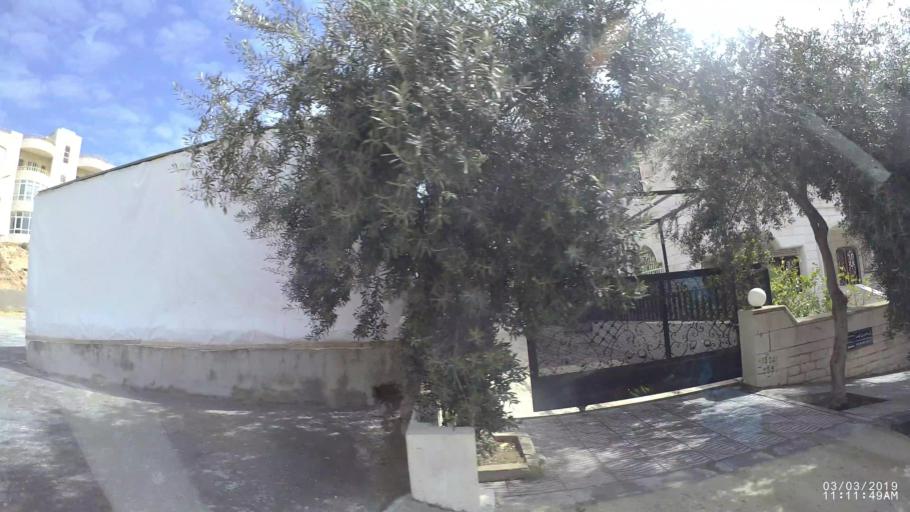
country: JO
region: Amman
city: Amman
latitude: 31.9976
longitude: 35.9160
